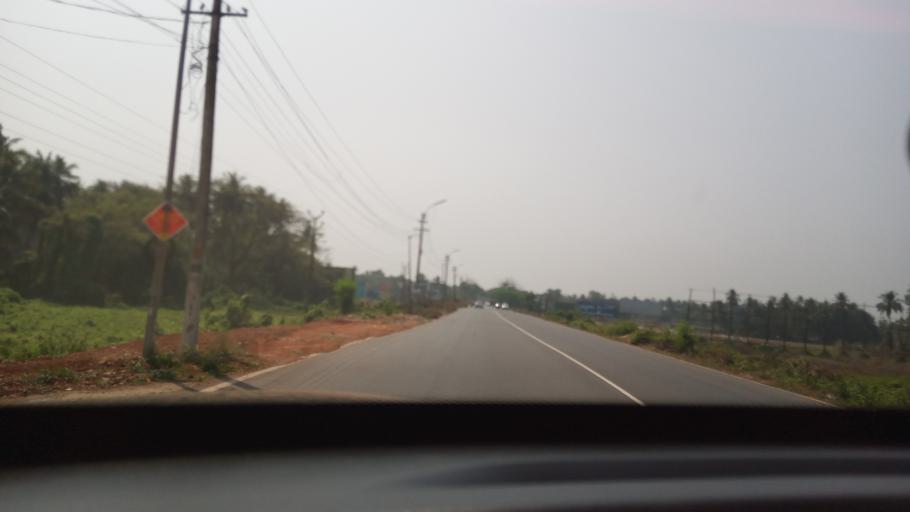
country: IN
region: Goa
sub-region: South Goa
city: Sancoale
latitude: 15.3530
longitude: 73.9277
